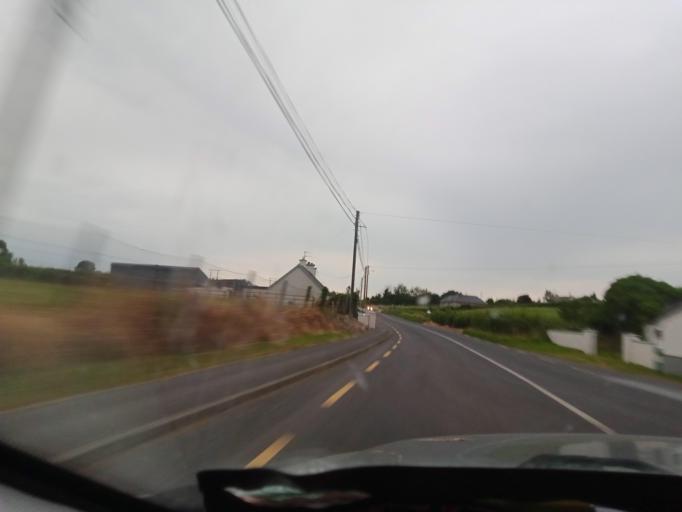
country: IE
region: Leinster
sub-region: Uibh Fhaili
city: Tullamore
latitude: 53.1467
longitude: -7.4846
